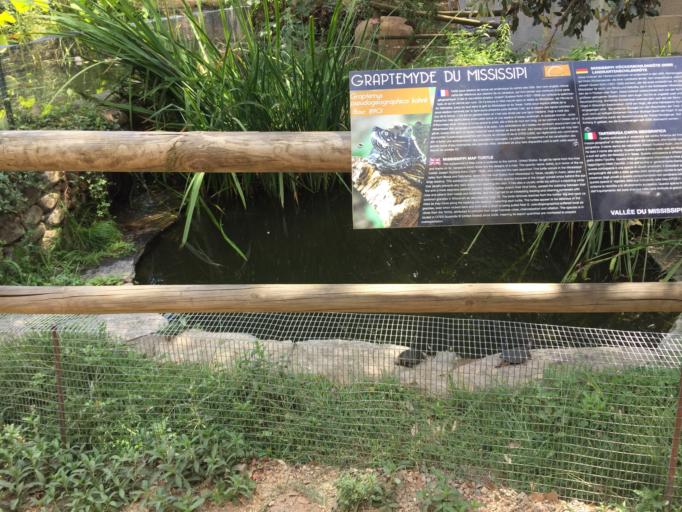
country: FR
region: Corsica
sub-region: Departement de la Corse-du-Sud
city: Peri
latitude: 42.0270
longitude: 8.9075
